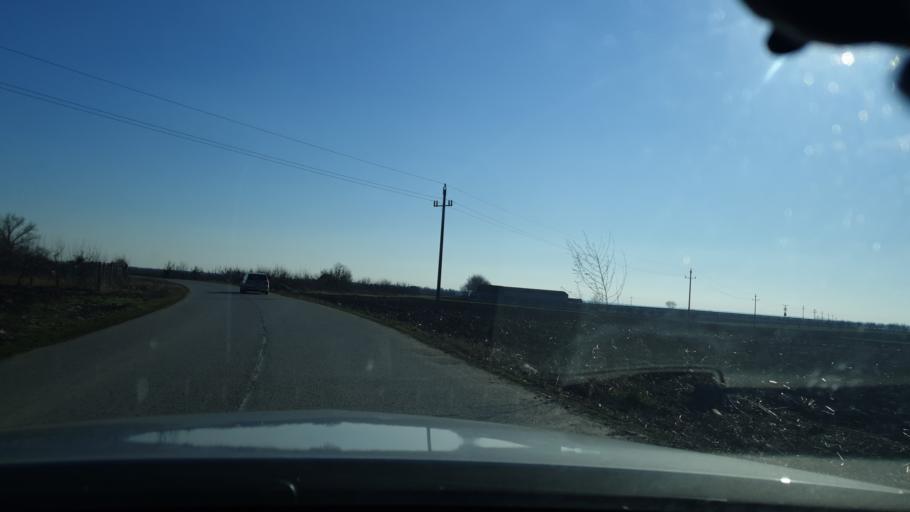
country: RS
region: Autonomna Pokrajina Vojvodina
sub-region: Sremski Okrug
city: Ruma
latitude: 45.0433
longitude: 19.8043
